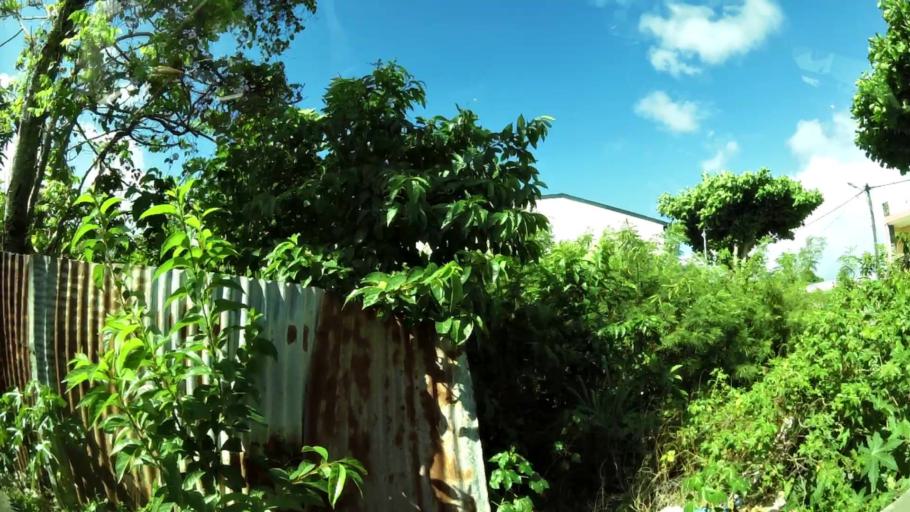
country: GP
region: Guadeloupe
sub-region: Guadeloupe
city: Port-Louis
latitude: 16.4165
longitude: -61.5311
